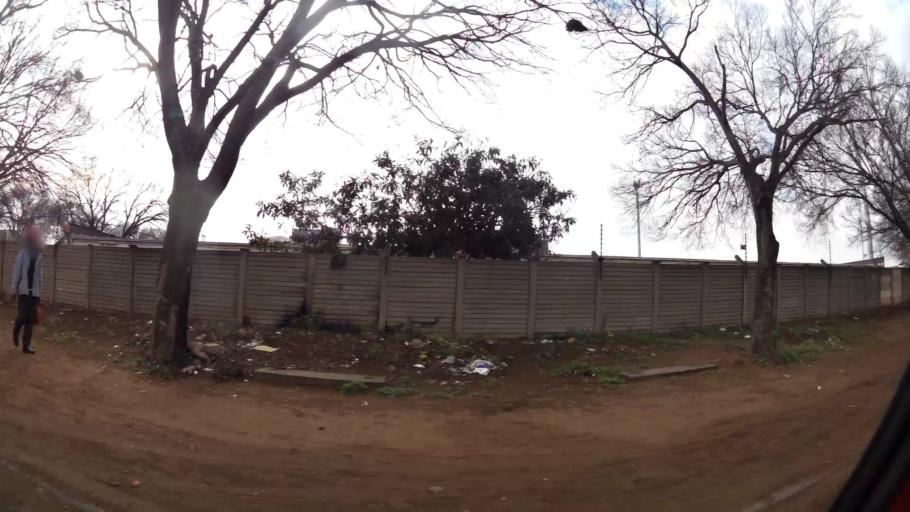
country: ZA
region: Gauteng
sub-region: Sedibeng District Municipality
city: Vanderbijlpark
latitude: -26.6891
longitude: 27.8132
